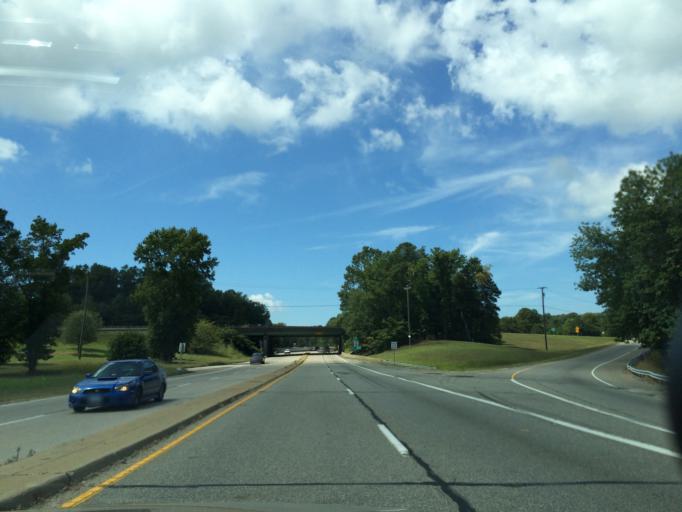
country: US
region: Virginia
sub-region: York County
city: Yorktown
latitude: 37.1726
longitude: -76.5640
